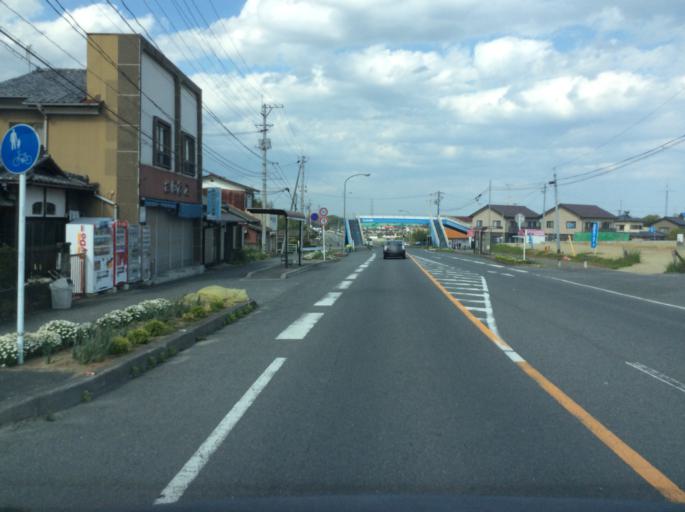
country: JP
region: Fukushima
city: Iwaki
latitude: 36.9273
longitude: 140.8214
